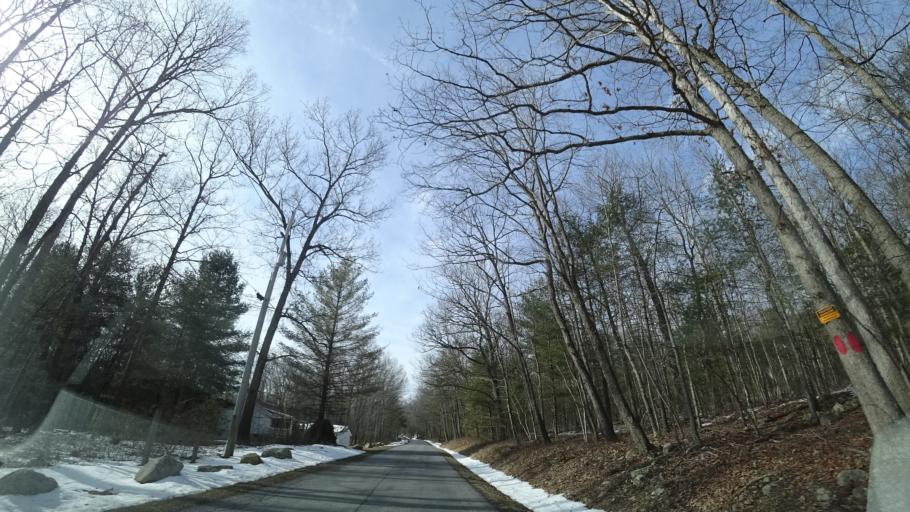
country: US
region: Virginia
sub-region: Shenandoah County
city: Edinburg
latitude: 38.9601
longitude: -78.6821
